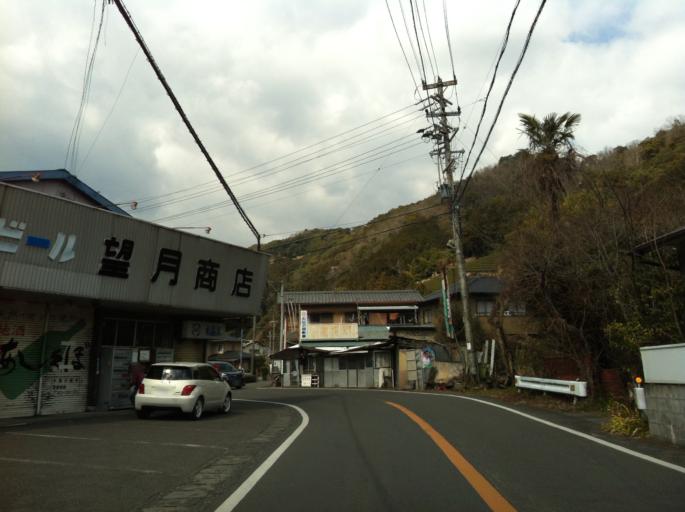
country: JP
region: Shizuoka
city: Shizuoka-shi
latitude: 35.0445
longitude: 138.3615
